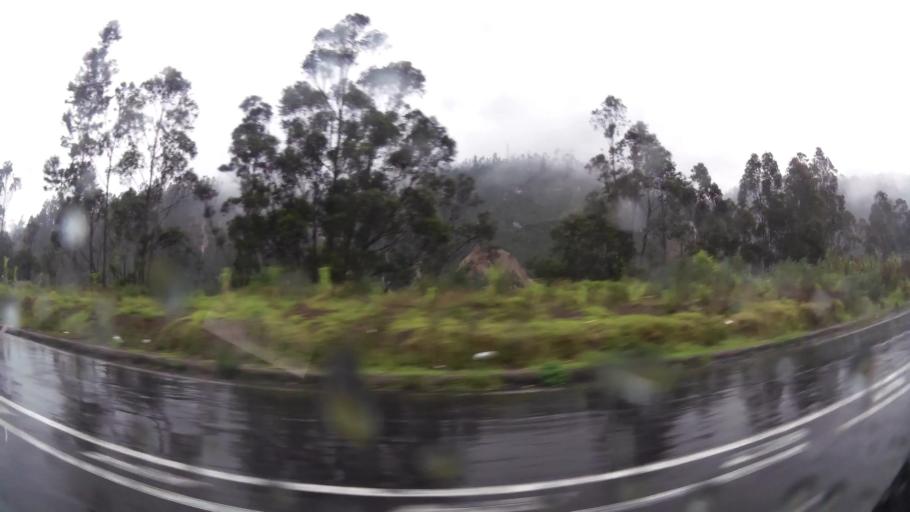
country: EC
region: Pichincha
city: Quito
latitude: -0.1418
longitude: -78.4437
